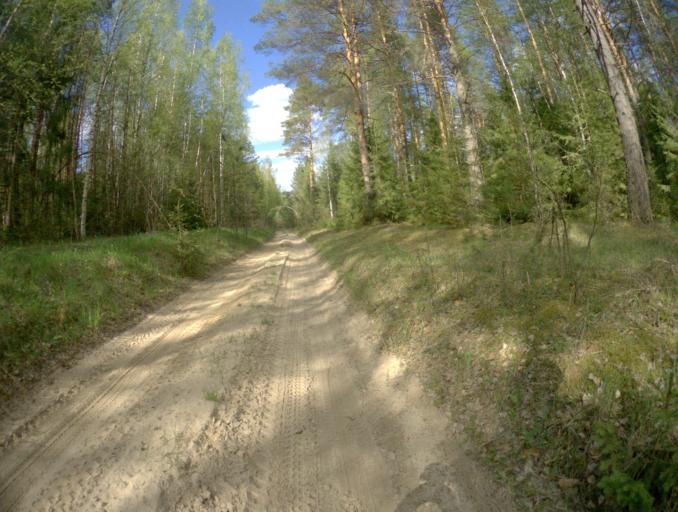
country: RU
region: Vladimir
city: Golovino
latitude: 55.8970
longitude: 40.4243
